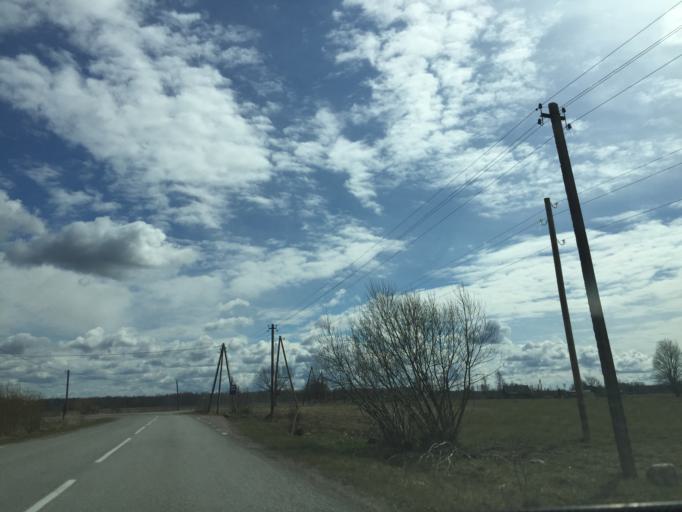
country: LV
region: Salacgrivas
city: Salacgriva
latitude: 57.7444
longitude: 24.3941
